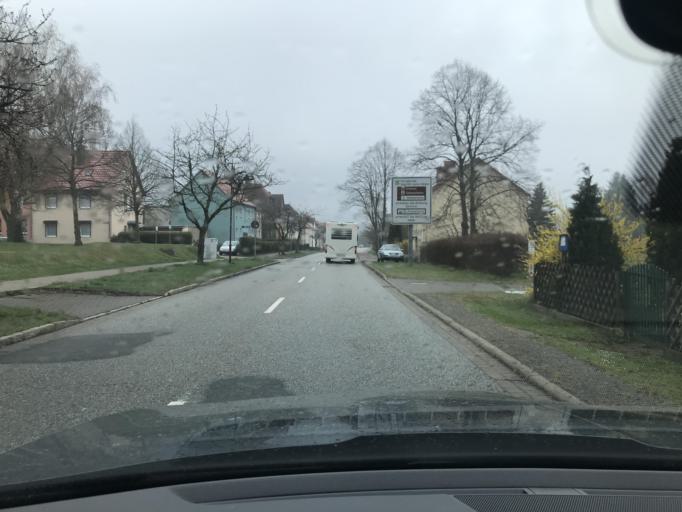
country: DE
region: Saxony-Anhalt
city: Harzgerode
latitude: 51.6486
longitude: 11.1399
